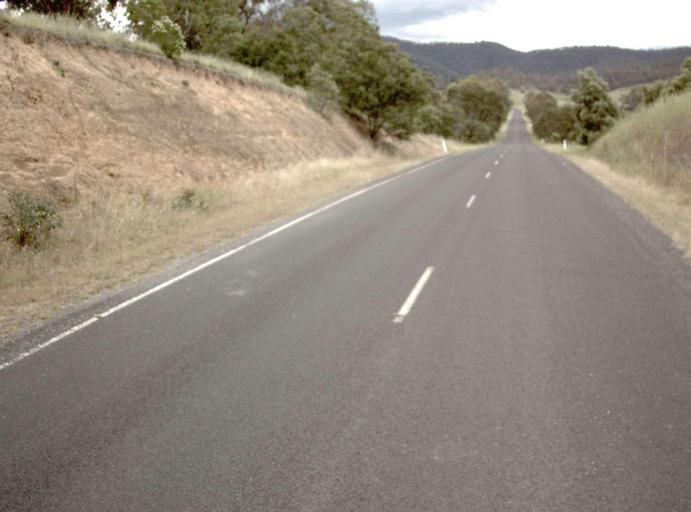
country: AU
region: Victoria
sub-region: East Gippsland
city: Bairnsdale
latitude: -37.5605
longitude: 147.1944
